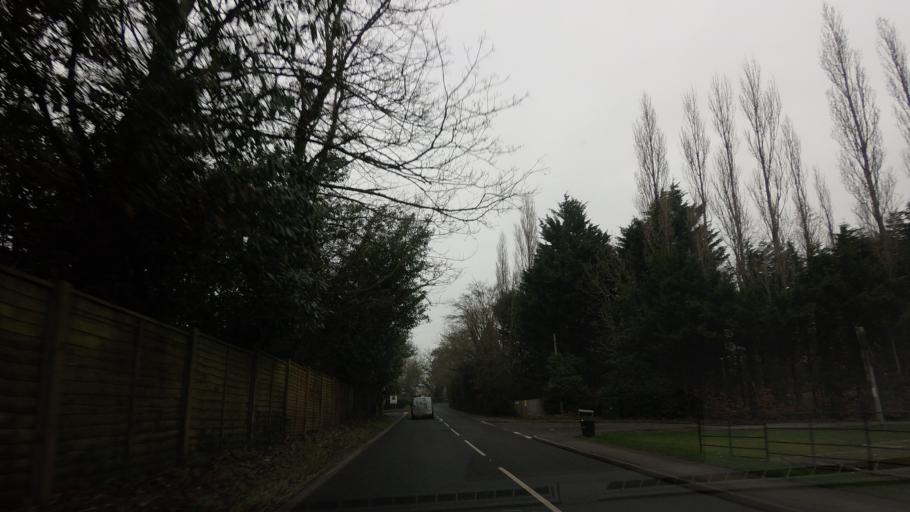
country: GB
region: England
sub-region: Kent
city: Hawkhurst
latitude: 51.0585
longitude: 0.5055
